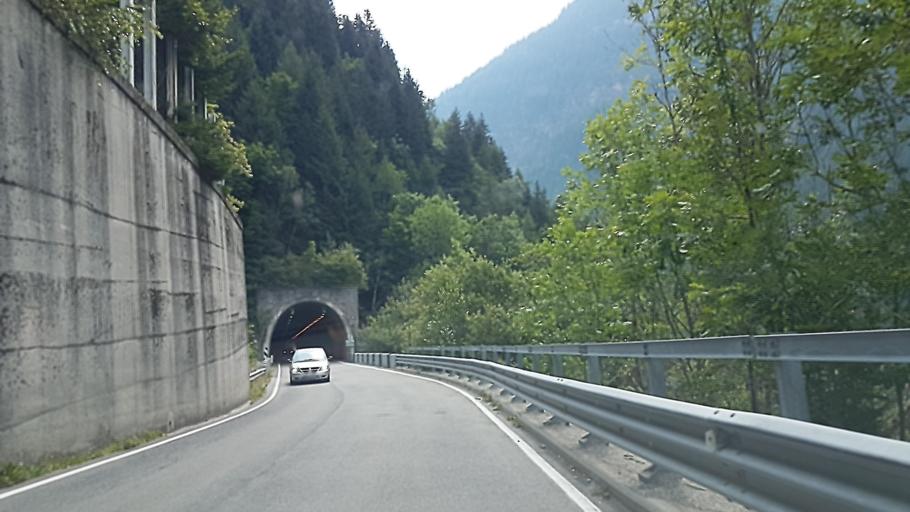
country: IT
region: Lombardy
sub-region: Provincia di Sondrio
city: Campodolcino
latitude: 46.3840
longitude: 9.3556
